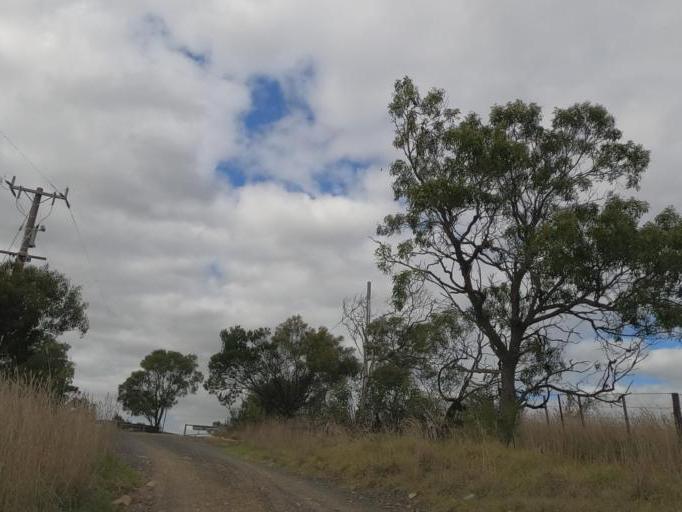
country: AU
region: Victoria
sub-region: Hume
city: Greenvale
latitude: -37.5617
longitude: 144.8589
